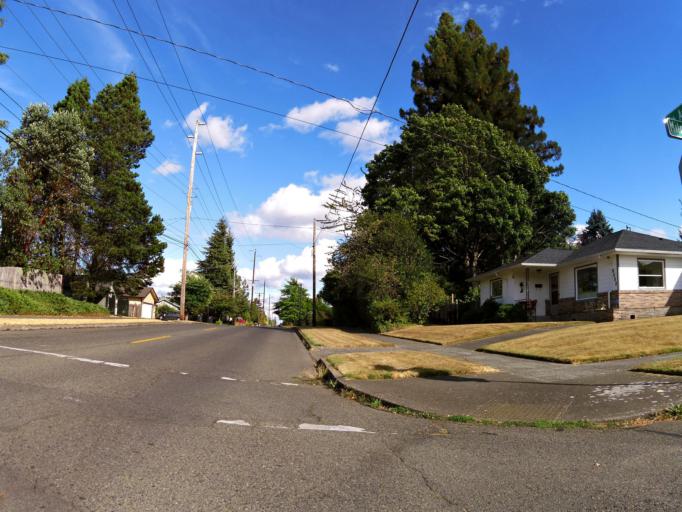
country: US
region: Washington
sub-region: Thurston County
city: Olympia
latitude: 47.0444
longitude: -122.9237
